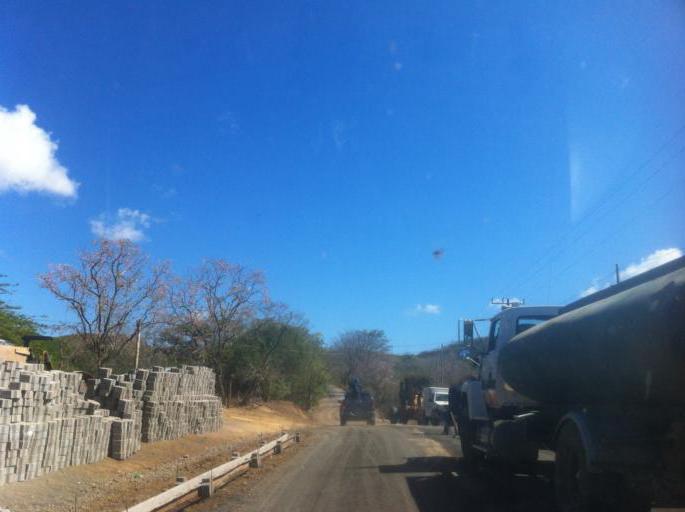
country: NI
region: Rivas
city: Tola
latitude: 11.3965
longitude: -85.9908
